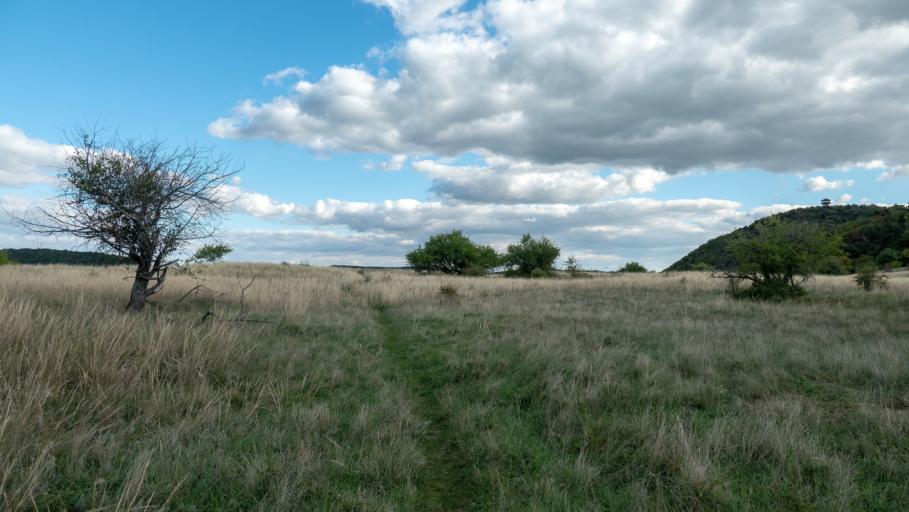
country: HU
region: Veszprem
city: Tihany
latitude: 46.9183
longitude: 17.8544
